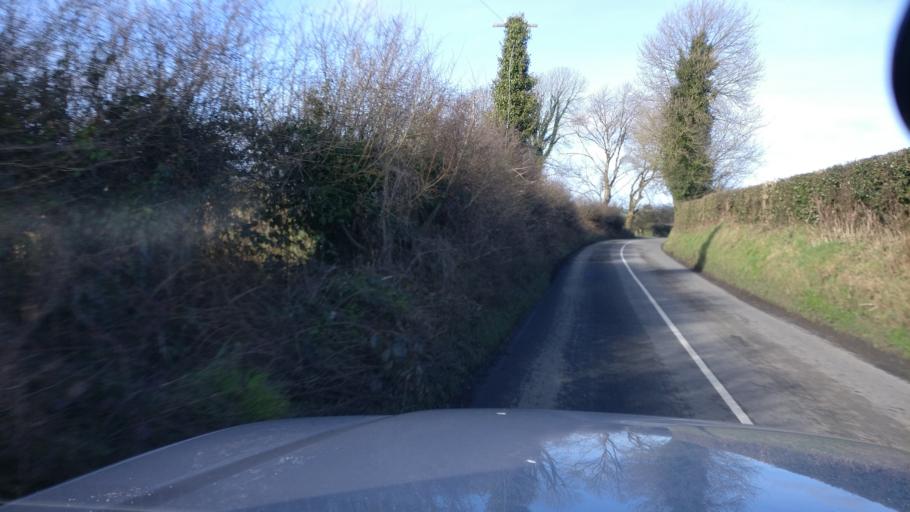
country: IE
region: Leinster
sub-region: Kilkenny
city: Castlecomer
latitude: 52.8814
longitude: -7.1631
